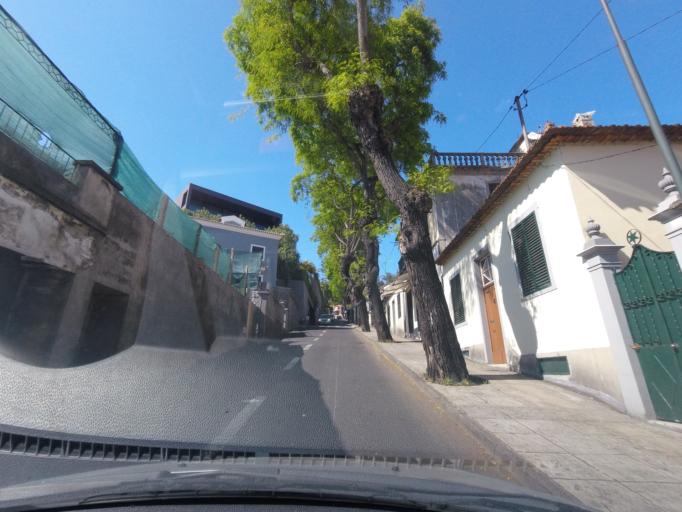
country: PT
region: Madeira
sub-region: Funchal
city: Nossa Senhora do Monte
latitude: 32.6588
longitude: -16.9031
